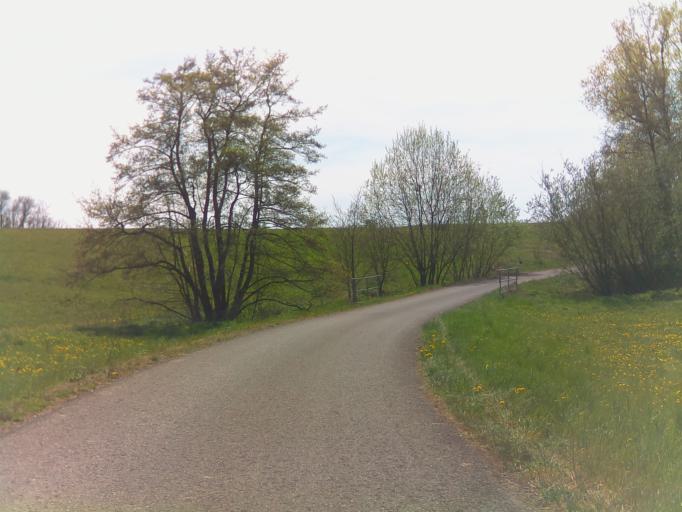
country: DE
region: Thuringia
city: Veilsdorf
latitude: 50.3728
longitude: 10.7676
